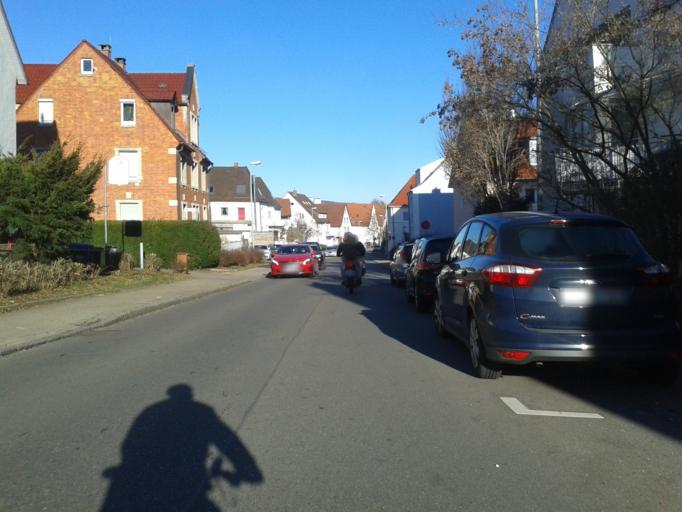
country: DE
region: Baden-Wuerttemberg
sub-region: Tuebingen Region
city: Ulm
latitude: 48.3902
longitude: 9.9597
